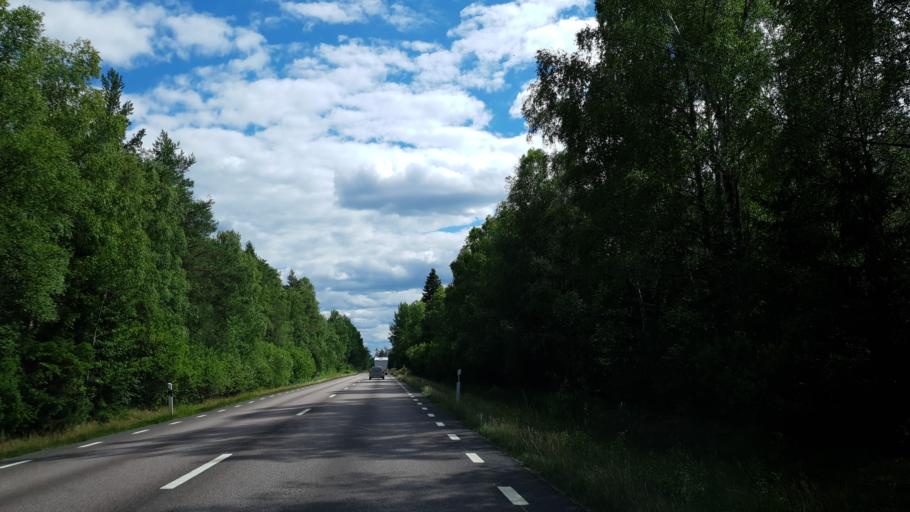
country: SE
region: Kronoberg
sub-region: Lessebo Kommun
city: Lessebo
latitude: 56.8416
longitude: 15.3905
